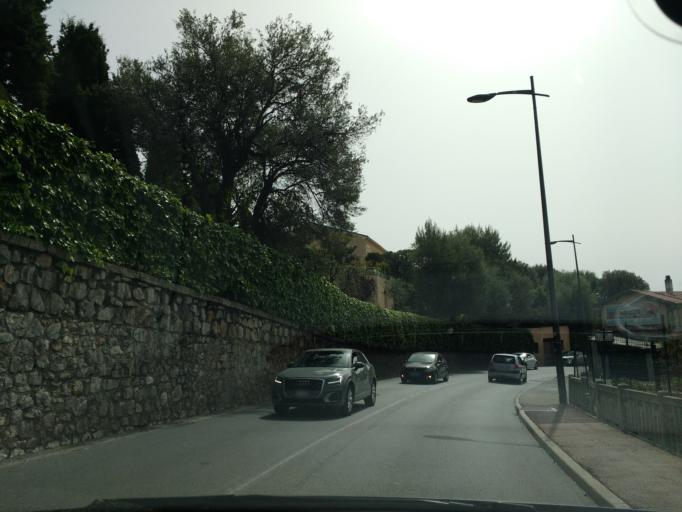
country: FR
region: Provence-Alpes-Cote d'Azur
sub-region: Departement des Alpes-Maritimes
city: Roquebrune-Cap-Martin
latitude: 43.7624
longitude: 7.4726
